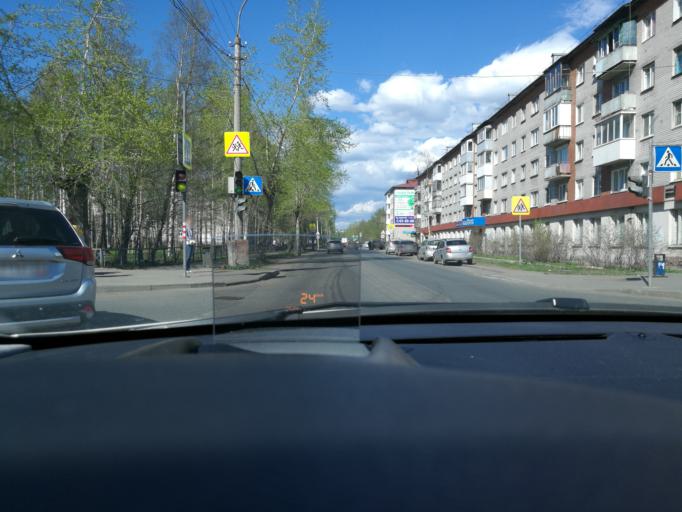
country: RU
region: Arkhangelskaya
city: Arkhangel'sk
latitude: 64.5497
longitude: 40.5355
